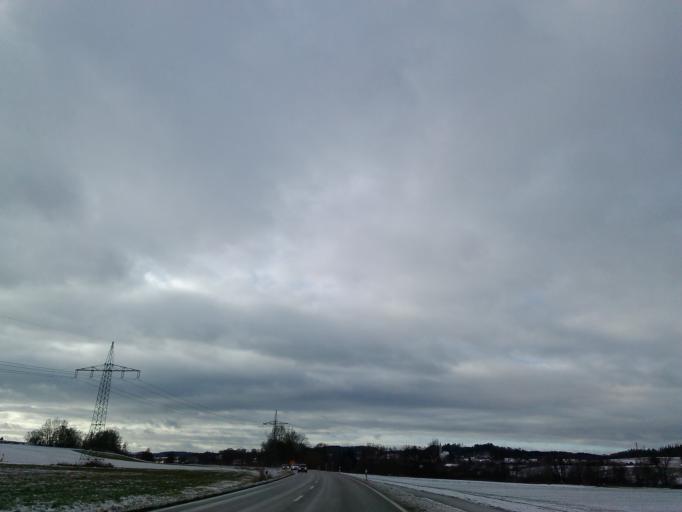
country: DE
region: Bavaria
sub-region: Swabia
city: Zusmarshausen
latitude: 48.3874
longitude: 10.5858
